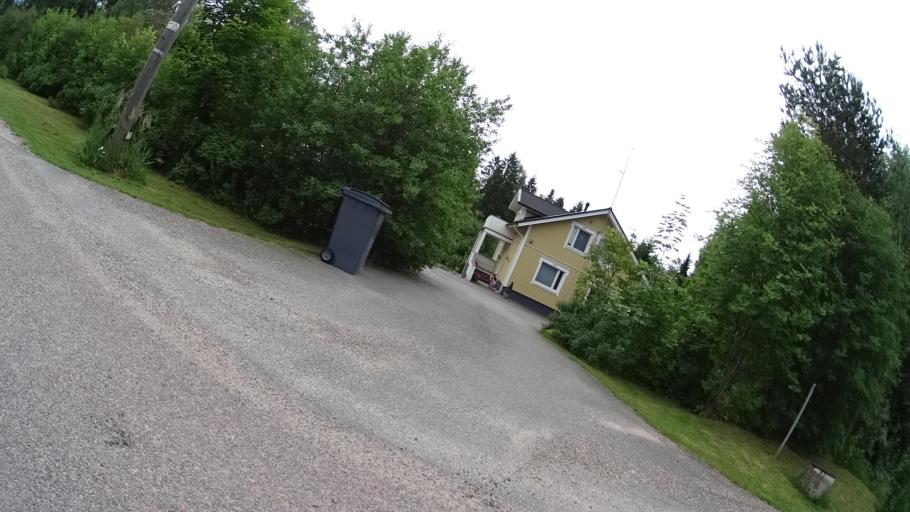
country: FI
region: Uusimaa
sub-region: Helsinki
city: Kauniainen
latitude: 60.3076
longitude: 24.7283
